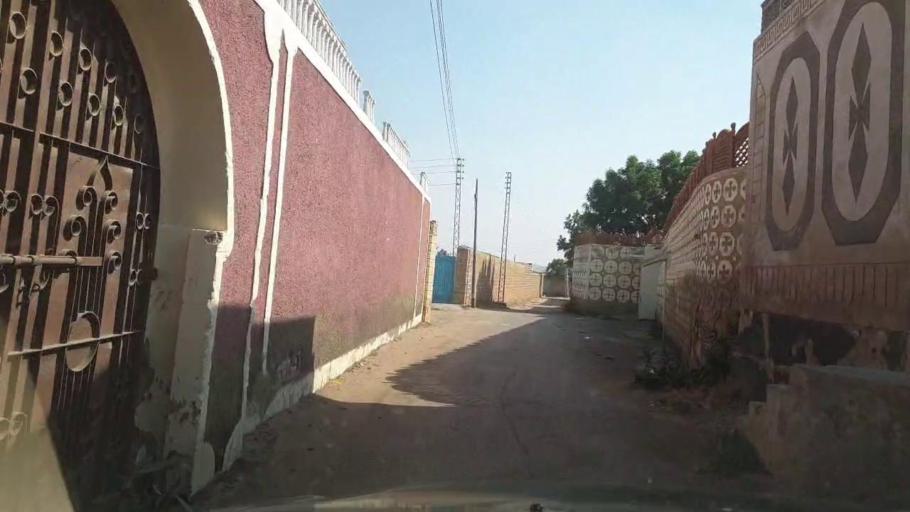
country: PK
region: Sindh
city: Jamshoro
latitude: 25.4090
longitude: 67.7870
